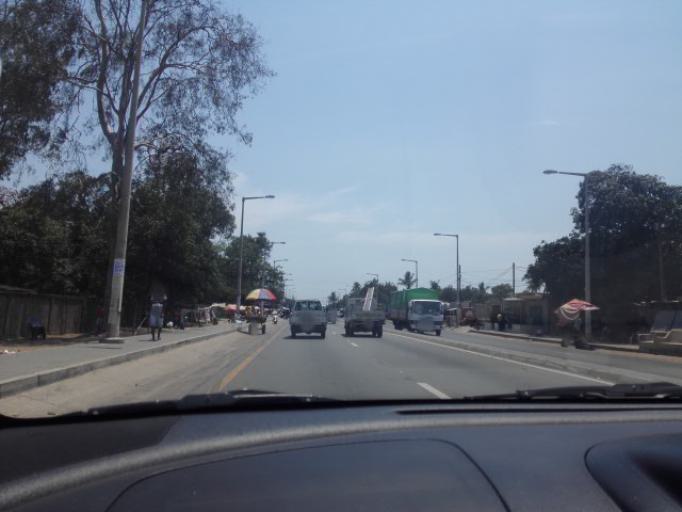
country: MZ
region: Maputo City
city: Maputo
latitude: -25.9252
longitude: 32.5589
